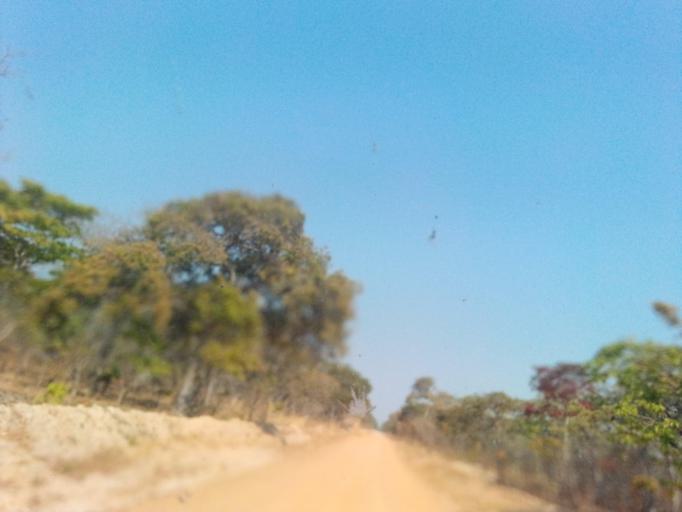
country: ZM
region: Northern
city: Mpika
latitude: -12.2297
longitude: 30.9180
